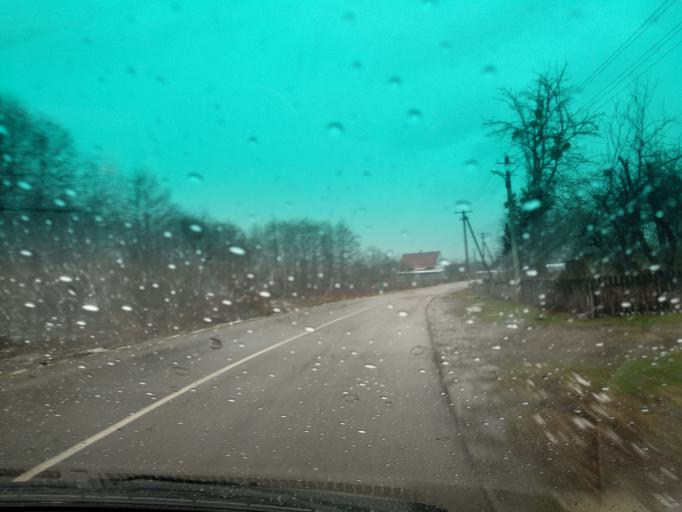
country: RU
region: Krasnodarskiy
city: Khadyzhensk
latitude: 44.2516
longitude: 39.3692
